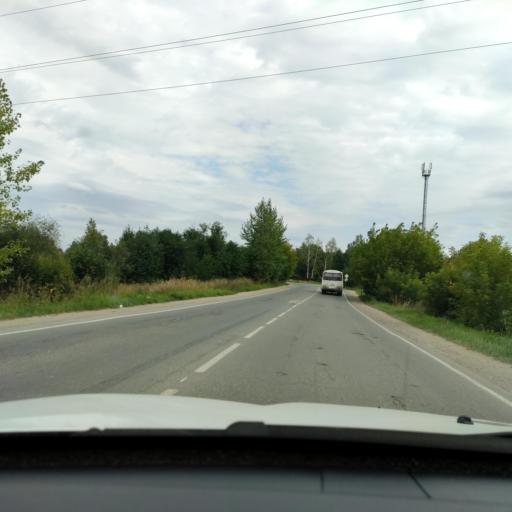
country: RU
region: Perm
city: Krasnokamsk
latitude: 58.0873
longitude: 55.7963
